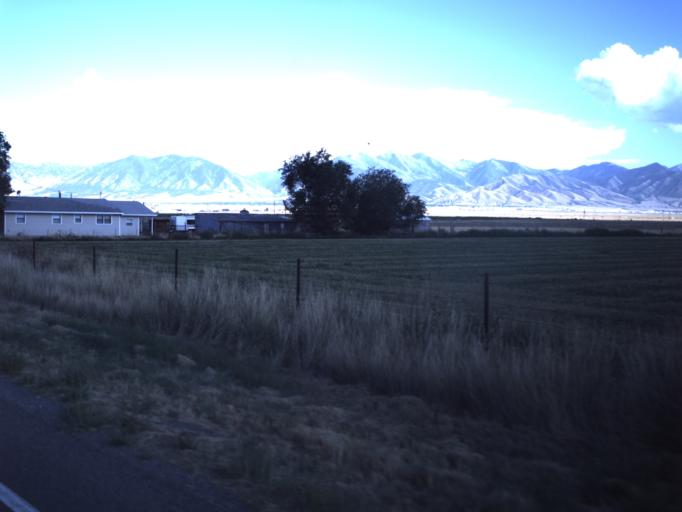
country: US
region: Utah
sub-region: Tooele County
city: Grantsville
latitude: 40.5996
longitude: -112.4194
